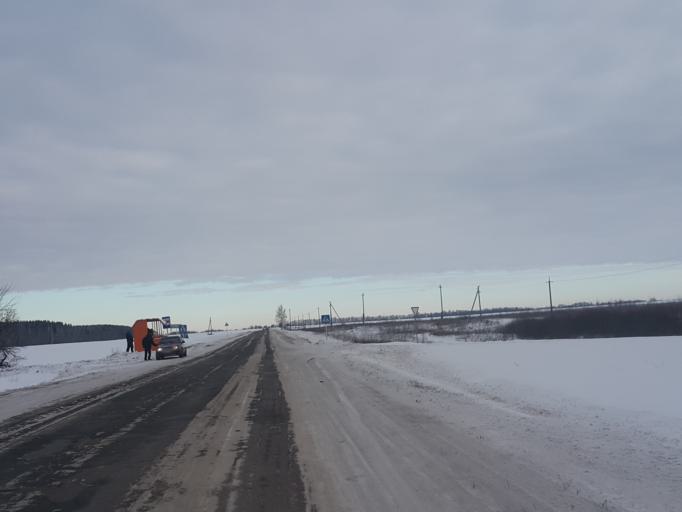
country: RU
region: Tambov
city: Novaya Lyada
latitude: 52.7524
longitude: 41.7173
